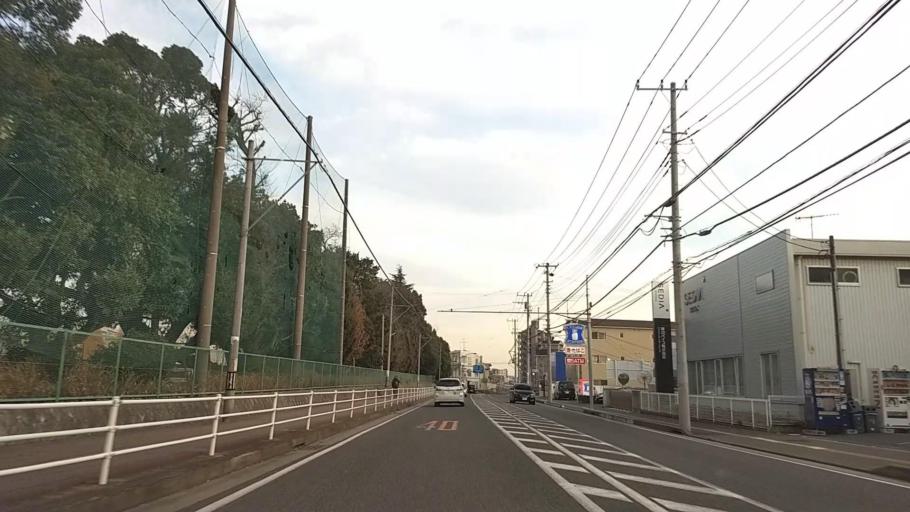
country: JP
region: Kanagawa
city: Atsugi
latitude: 35.4453
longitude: 139.3483
